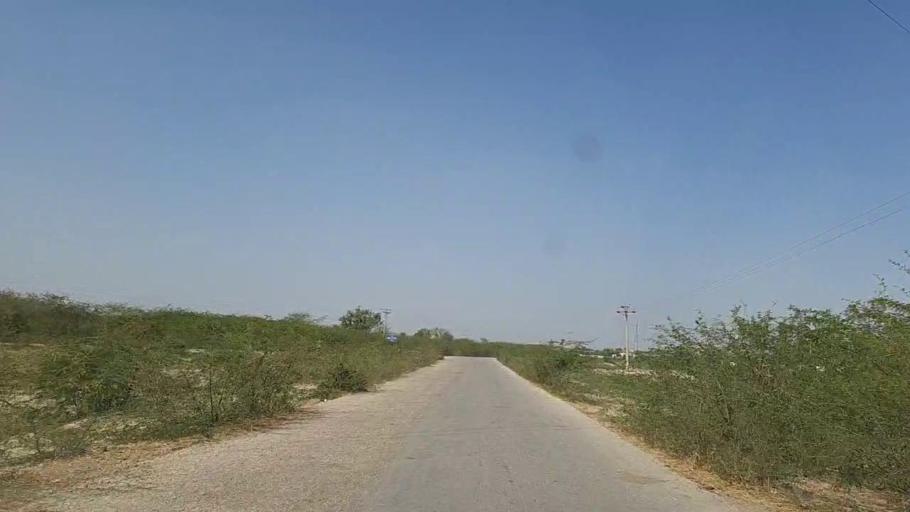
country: PK
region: Sindh
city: Naukot
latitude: 24.6498
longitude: 69.2879
